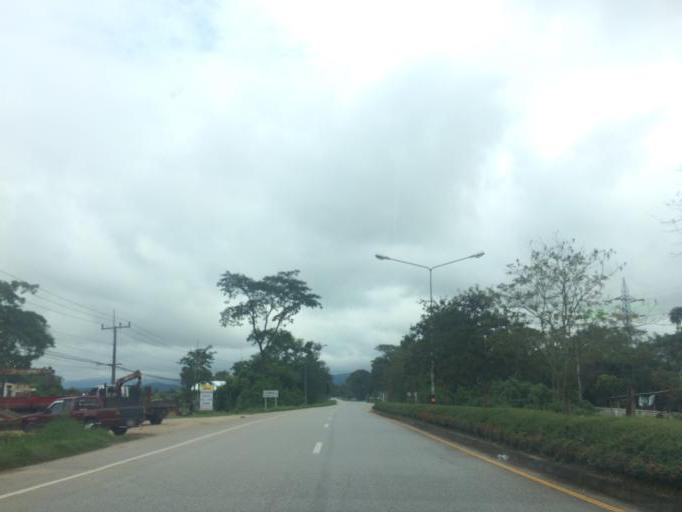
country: TH
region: Chiang Rai
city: Mae Lao
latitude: 19.7462
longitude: 99.6911
